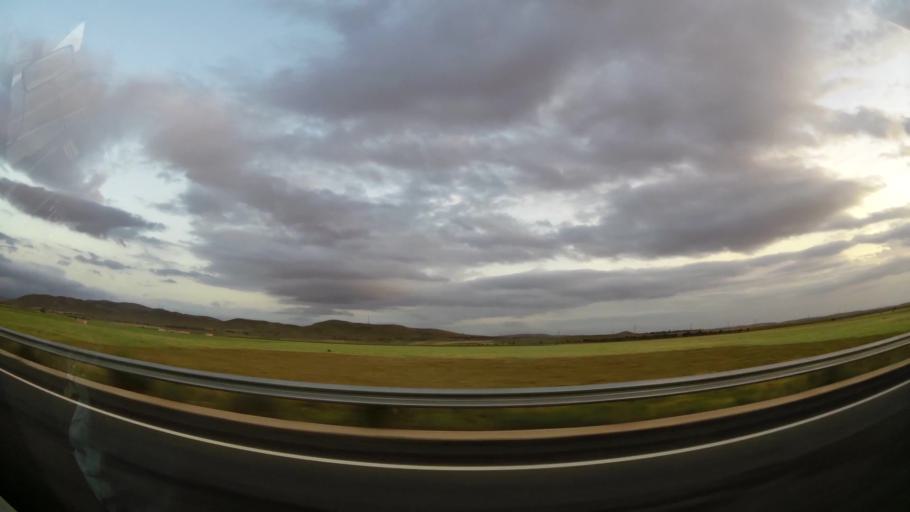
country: MA
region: Oriental
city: El Aioun
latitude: 34.5967
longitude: -2.7151
